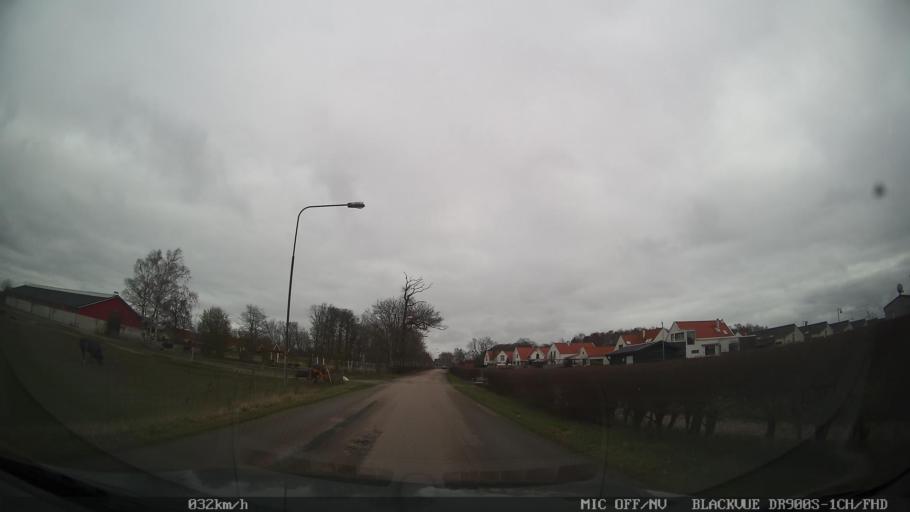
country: SE
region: Skane
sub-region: Helsingborg
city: Odakra
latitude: 56.0901
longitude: 12.6920
